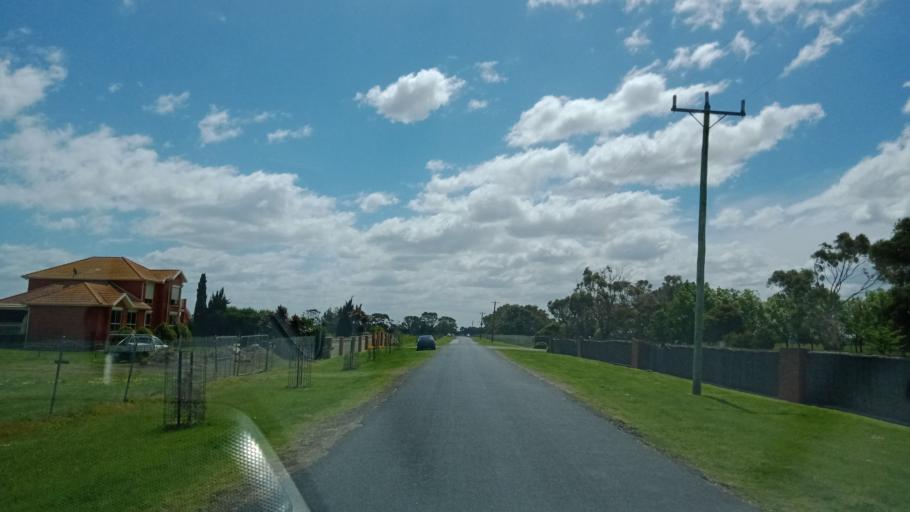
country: AU
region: Victoria
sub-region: Kingston
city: Chelsea Heights
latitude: -38.0408
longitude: 145.1452
